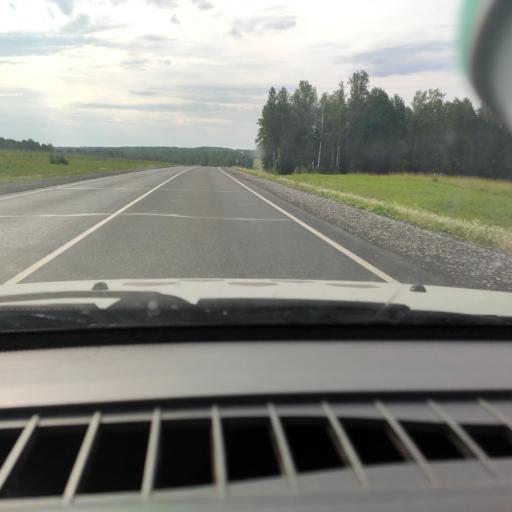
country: RU
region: Perm
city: Siva
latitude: 58.6365
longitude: 53.8519
